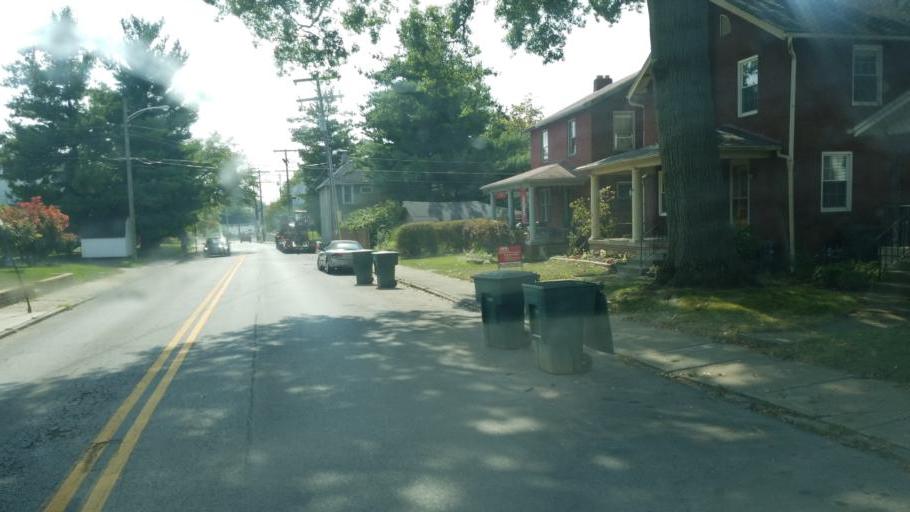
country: US
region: Ohio
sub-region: Franklin County
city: Grandview Heights
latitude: 40.0210
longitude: -83.0077
